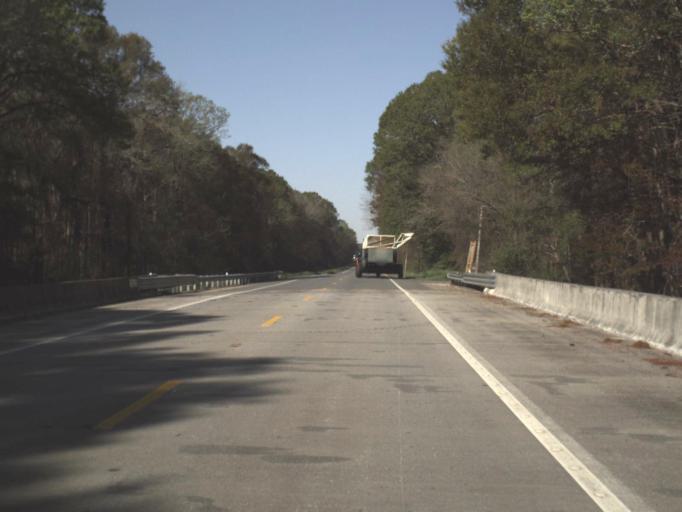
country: US
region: Florida
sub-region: Jackson County
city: Malone
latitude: 30.9473
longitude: -85.2594
